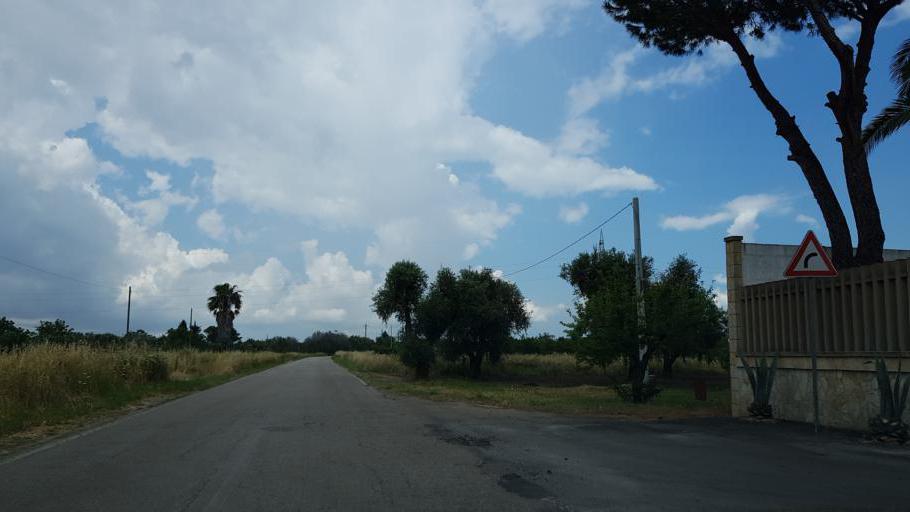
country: IT
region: Apulia
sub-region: Provincia di Brindisi
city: San Donaci
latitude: 40.4573
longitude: 17.9236
